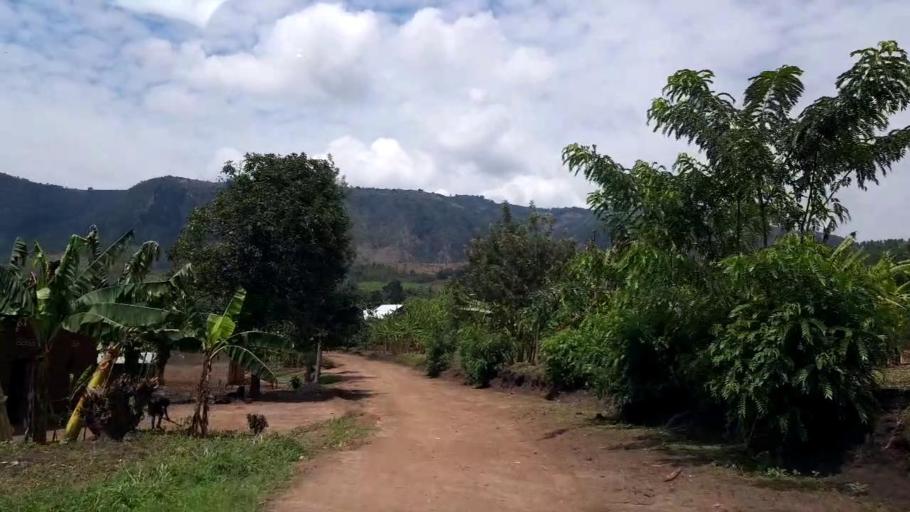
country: RW
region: Northern Province
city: Byumba
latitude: -1.4904
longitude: 30.1996
